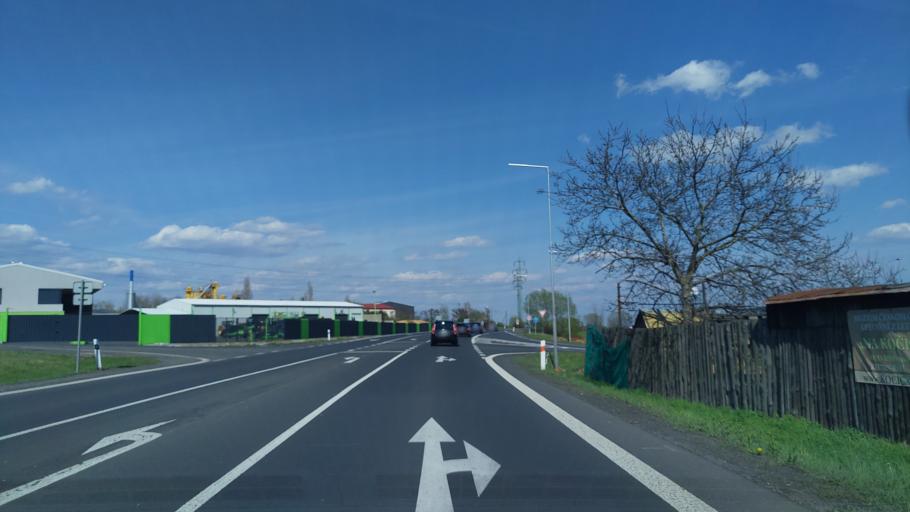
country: CZ
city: Krasna Lipa
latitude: 50.4512
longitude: 13.3624
